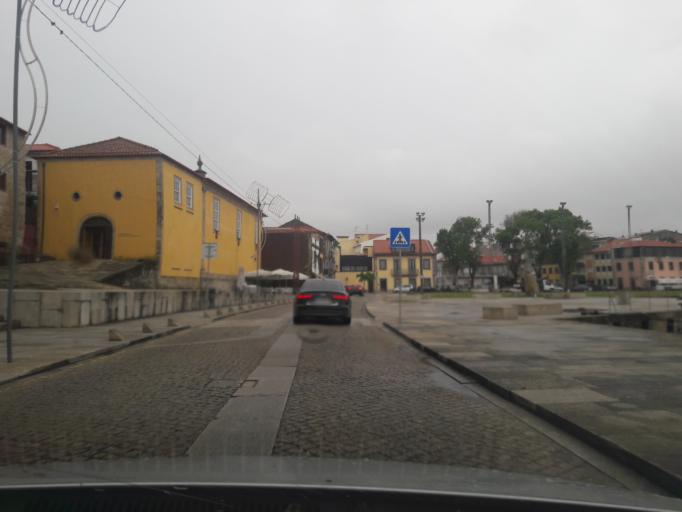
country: PT
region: Porto
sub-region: Vila do Conde
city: Vila do Conde
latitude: 41.3497
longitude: -8.7436
